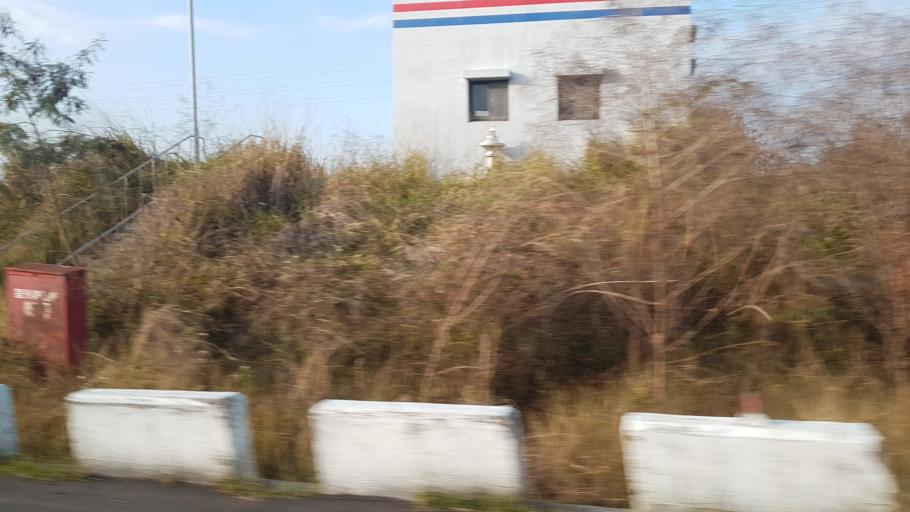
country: TW
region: Taiwan
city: Xinying
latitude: 23.3516
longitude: 120.3820
